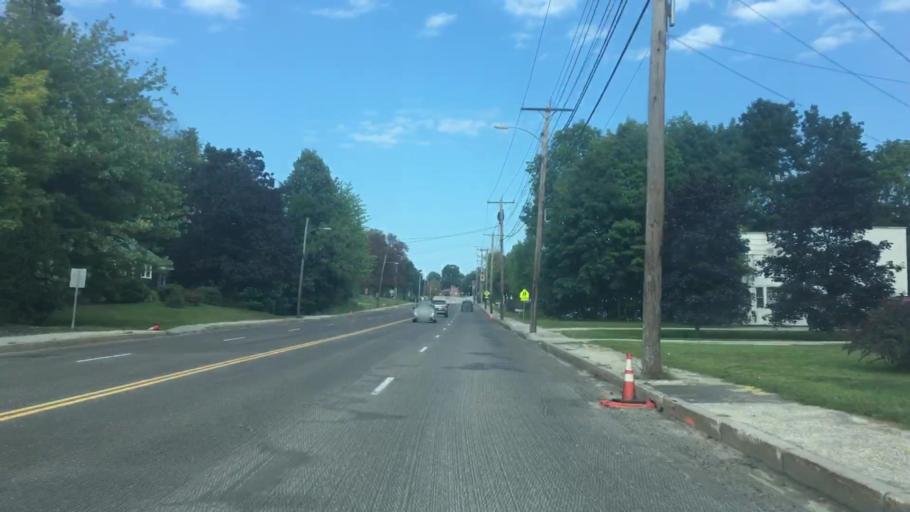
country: US
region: Maine
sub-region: Androscoggin County
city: Auburn
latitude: 44.0828
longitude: -70.2472
